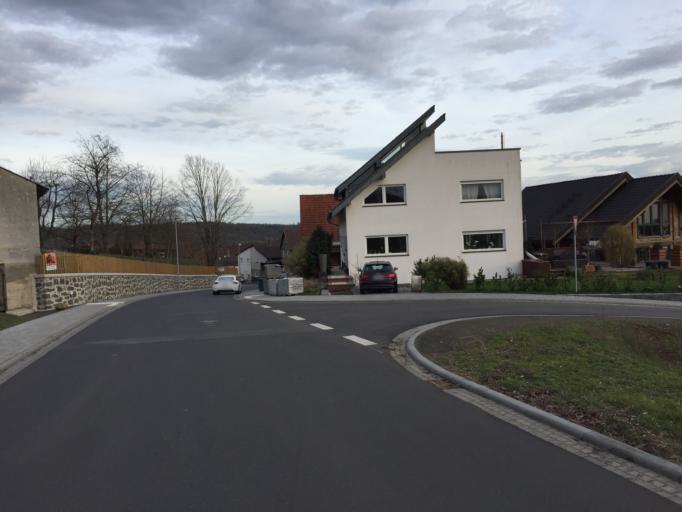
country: DE
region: Hesse
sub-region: Regierungsbezirk Giessen
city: Rabenau
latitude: 50.6916
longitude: 8.8370
